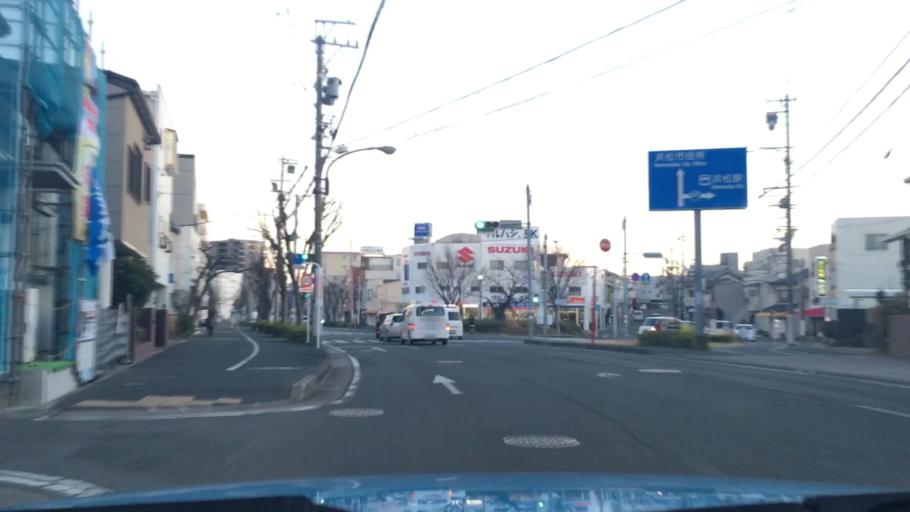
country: JP
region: Shizuoka
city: Hamamatsu
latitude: 34.7134
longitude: 137.7213
